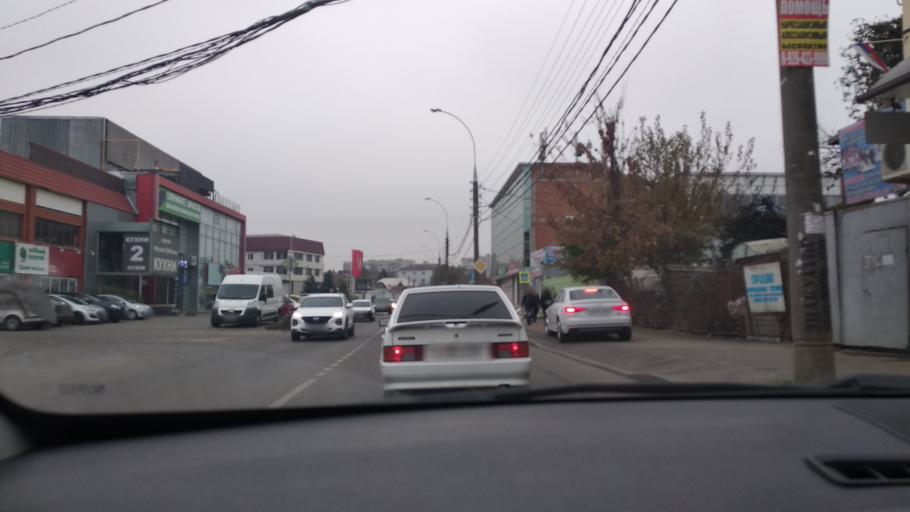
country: RU
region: Krasnodarskiy
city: Krasnodar
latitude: 45.0247
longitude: 39.0083
